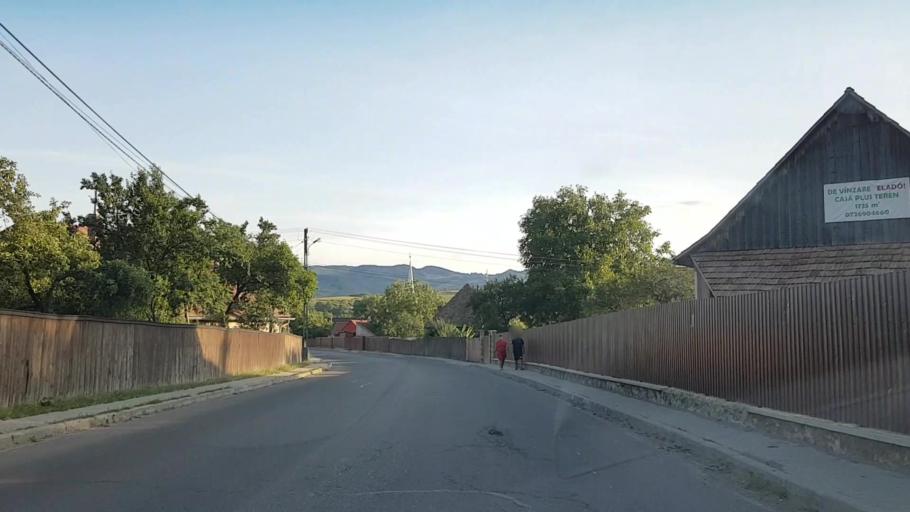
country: RO
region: Harghita
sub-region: Comuna Praid
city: Praid
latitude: 46.5563
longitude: 25.1298
